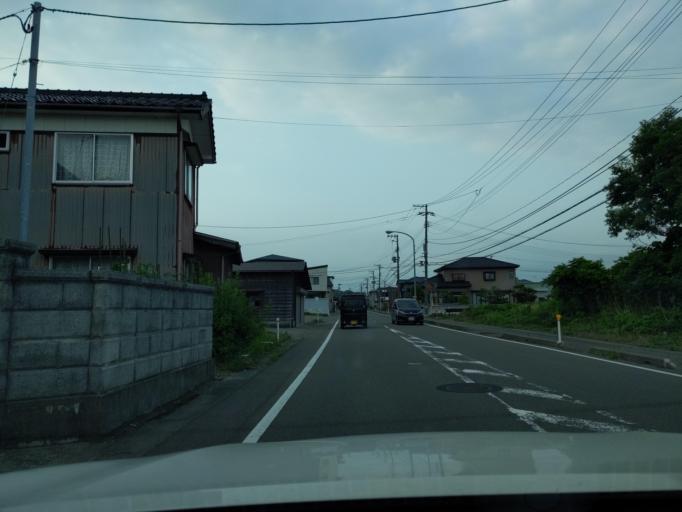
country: JP
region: Niigata
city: Kashiwazaki
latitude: 37.4139
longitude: 138.6105
